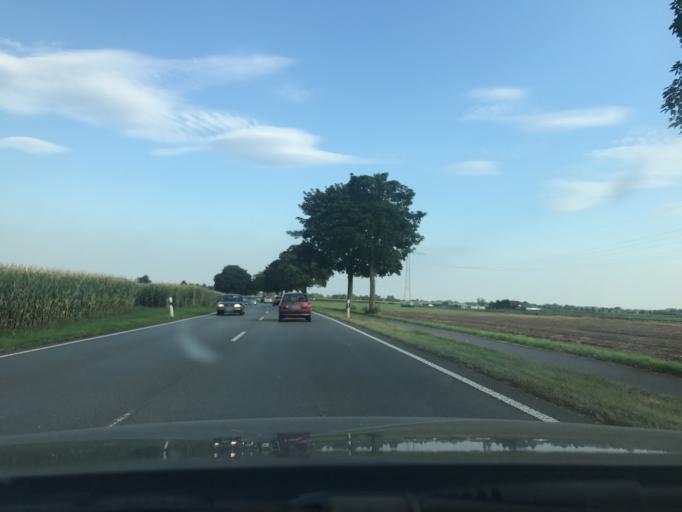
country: DE
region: North Rhine-Westphalia
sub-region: Regierungsbezirk Dusseldorf
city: Wachtendonk
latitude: 51.4497
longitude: 6.3898
